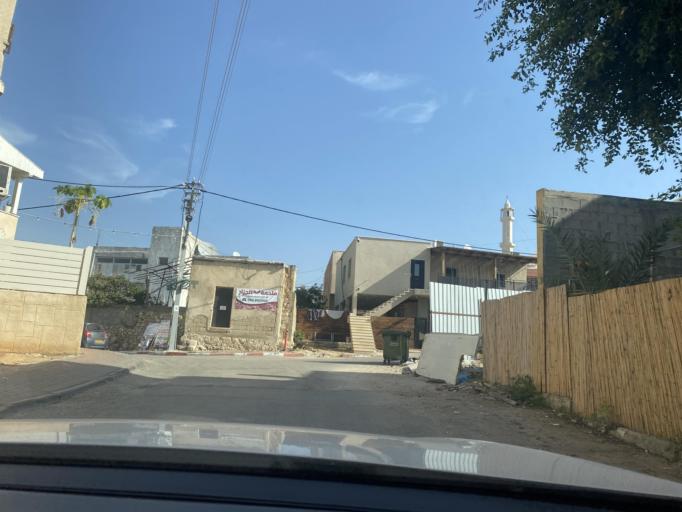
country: IL
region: Central District
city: Kafr Qasim
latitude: 32.1309
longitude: 34.9726
